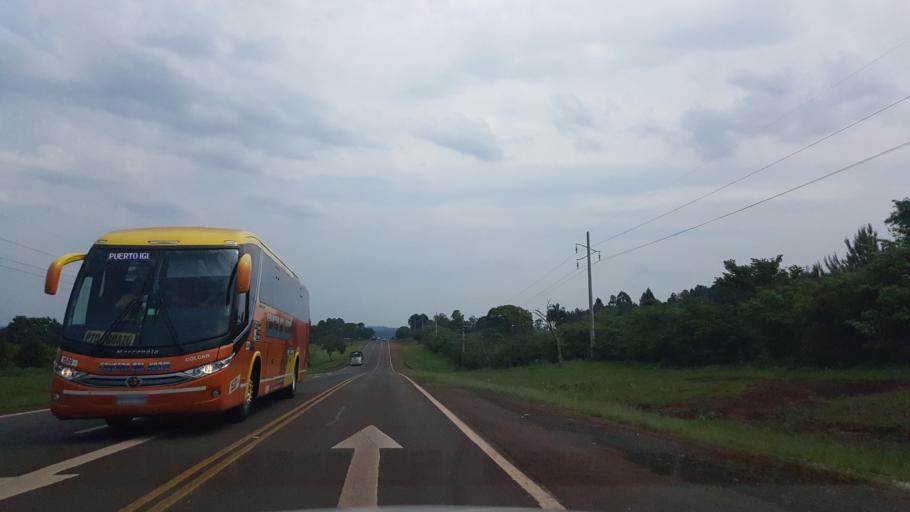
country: AR
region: Misiones
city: Capiovi
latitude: -26.9442
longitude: -55.0843
